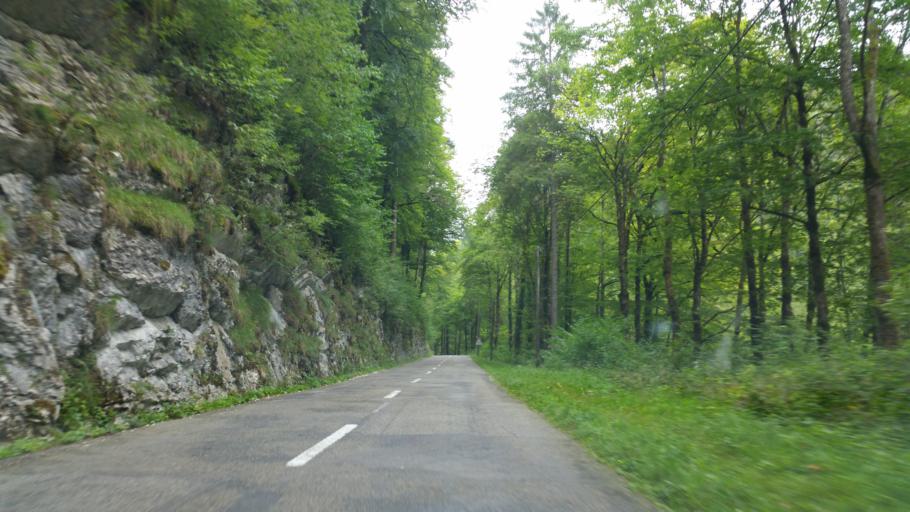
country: CH
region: Neuchatel
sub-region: La Chaux-de-Fonds District
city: La Chaux-de-Fonds
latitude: 47.1538
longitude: 6.8424
